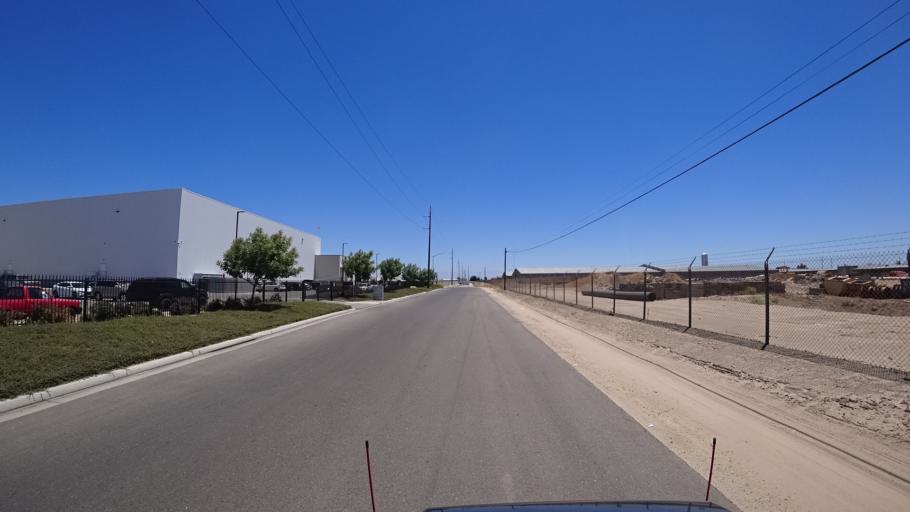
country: US
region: California
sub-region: Fresno County
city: Fresno
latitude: 36.6960
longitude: -119.7432
